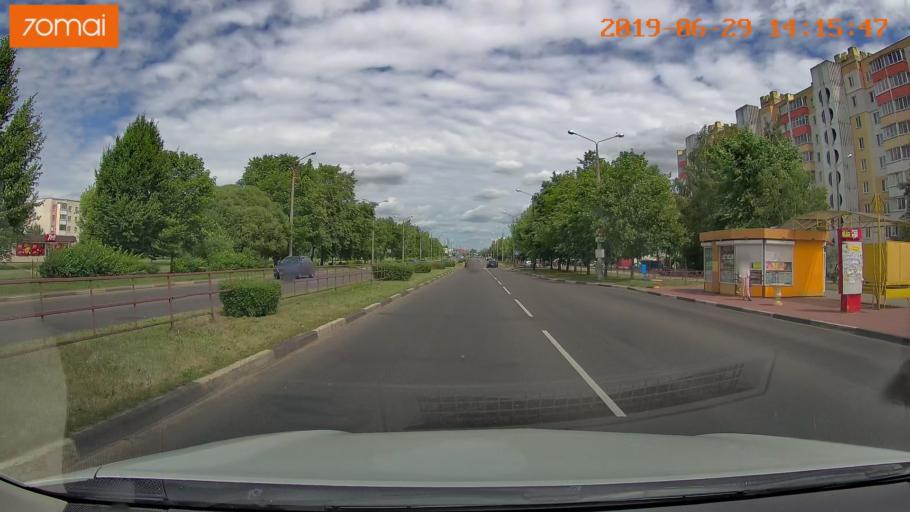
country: BY
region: Minsk
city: Salihorsk
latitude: 52.7935
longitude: 27.5258
